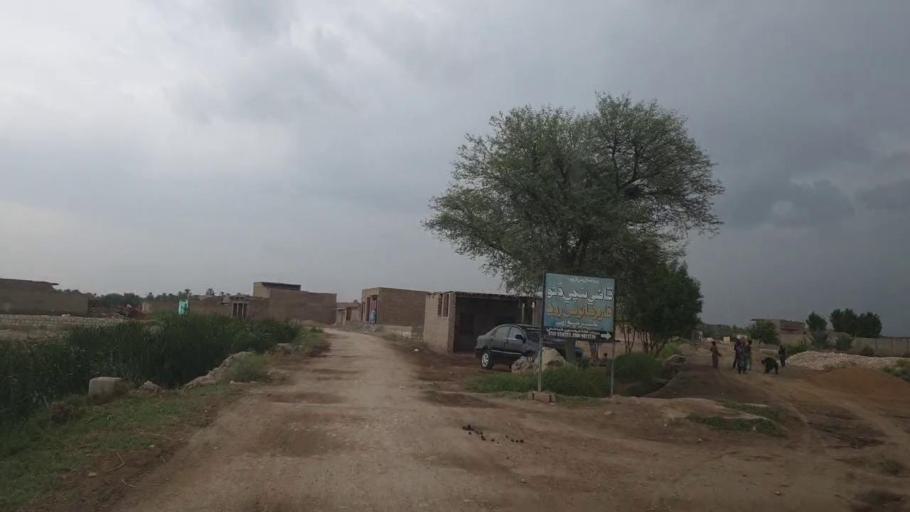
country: PK
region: Sindh
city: Khairpur
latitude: 27.5347
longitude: 68.7347
